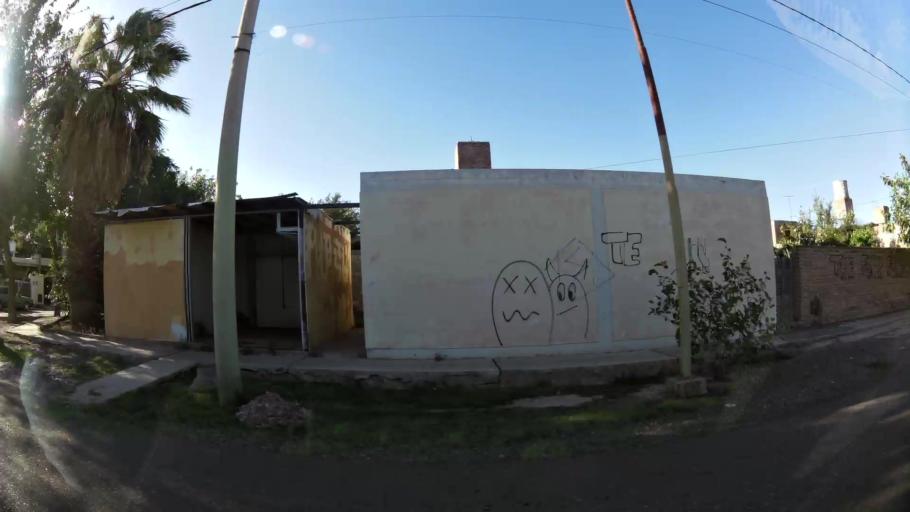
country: AR
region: San Juan
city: Villa Krause
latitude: -31.5509
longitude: -68.5194
